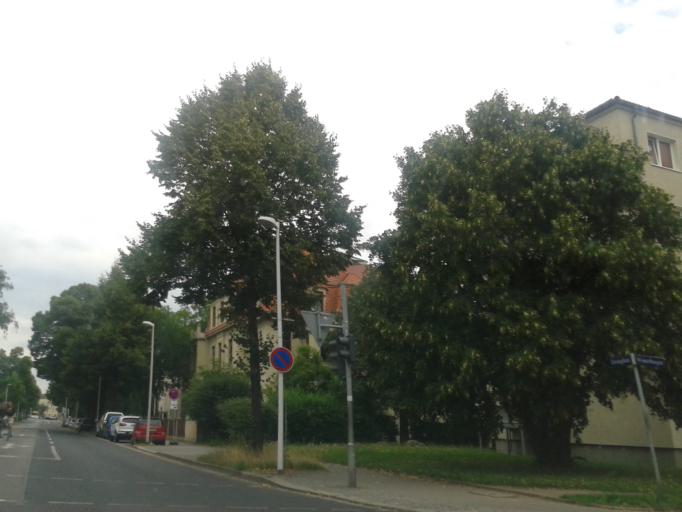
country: DE
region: Saxony
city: Dresden
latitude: 51.0309
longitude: 13.7805
